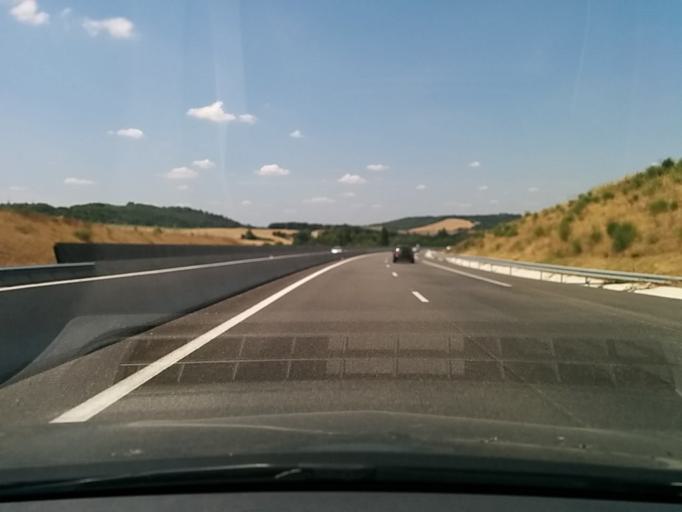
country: FR
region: Midi-Pyrenees
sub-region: Departement du Gers
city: Preignan
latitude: 43.6522
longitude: 0.6711
